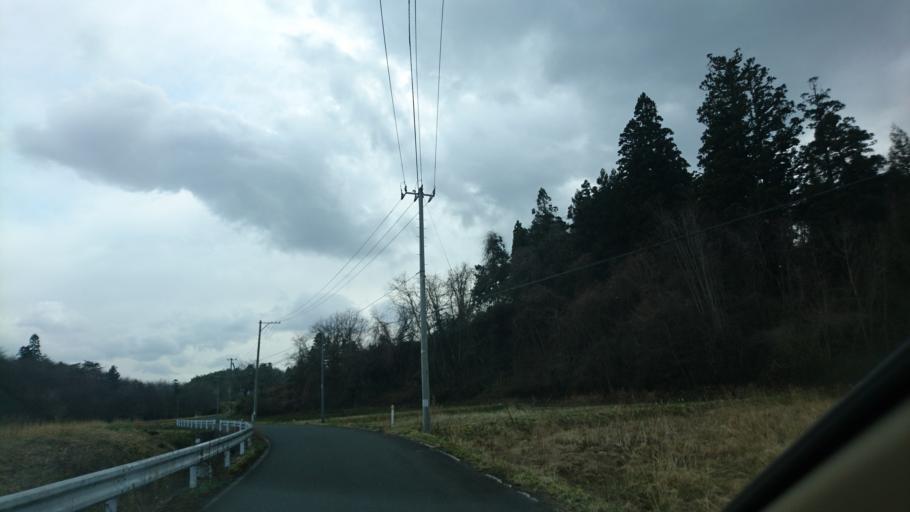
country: JP
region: Iwate
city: Ichinoseki
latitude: 38.8876
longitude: 141.1689
